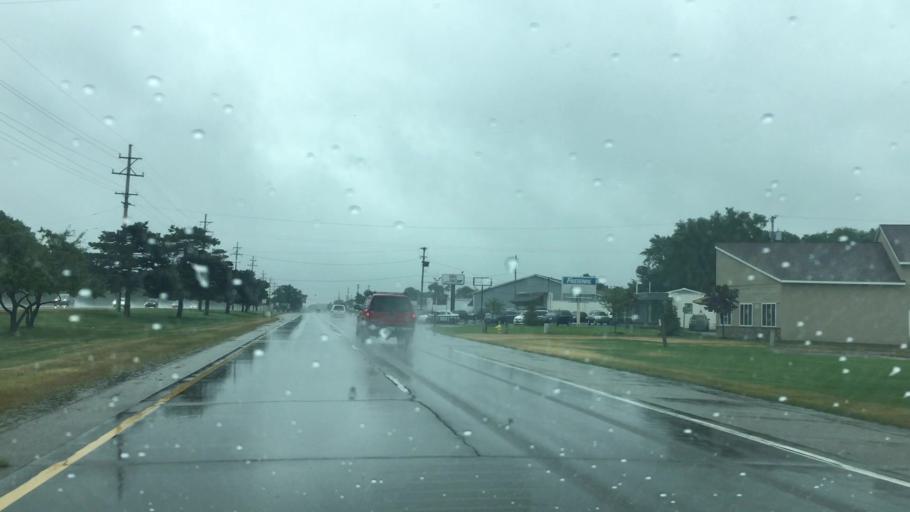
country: US
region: Michigan
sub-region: Ottawa County
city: Jenison
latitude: 42.8980
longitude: -85.8053
